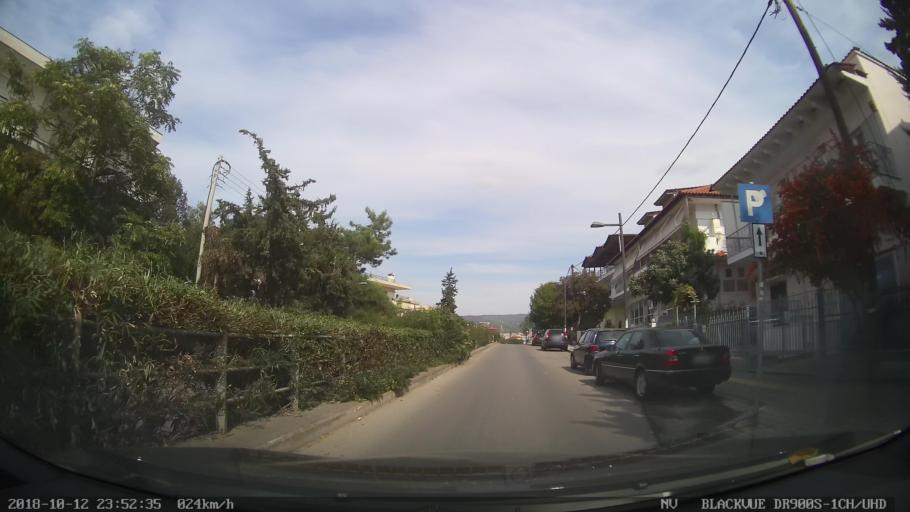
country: GR
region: Central Macedonia
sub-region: Nomos Thessalonikis
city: Pylaia
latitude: 40.5982
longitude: 22.9797
